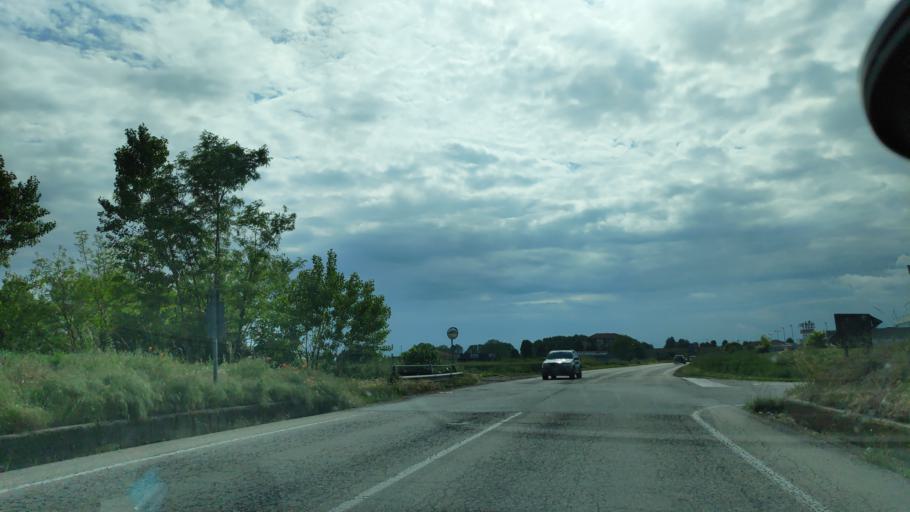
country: IT
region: Piedmont
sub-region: Provincia di Torino
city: Cambiano
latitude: 44.9648
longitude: 7.7821
